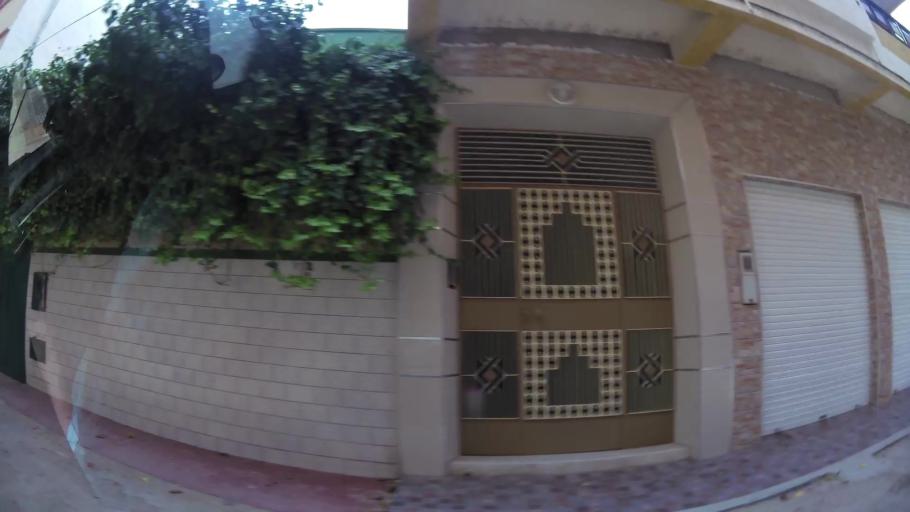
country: MA
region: Oriental
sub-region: Nador
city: Nador
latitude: 35.1647
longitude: -2.9262
